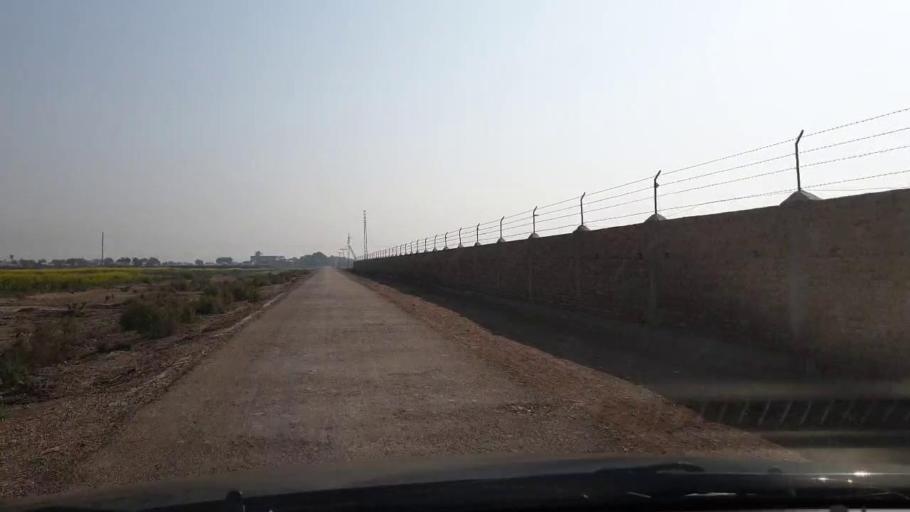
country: PK
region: Sindh
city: Sanghar
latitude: 25.9772
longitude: 68.9707
